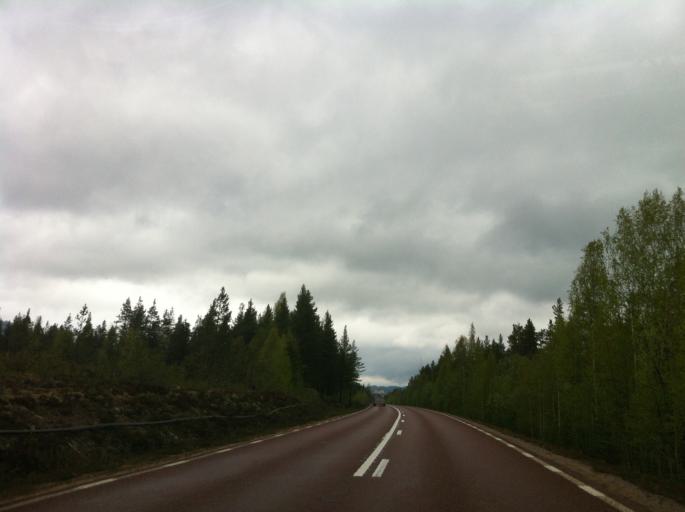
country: SE
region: Jaemtland
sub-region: Harjedalens Kommun
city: Sveg
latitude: 61.9199
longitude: 14.6162
